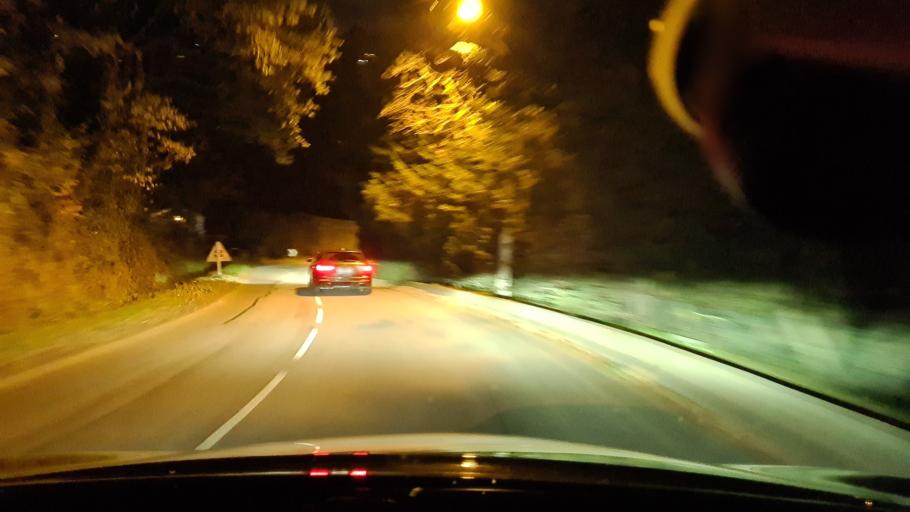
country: FR
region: Rhone-Alpes
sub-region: Departement du Rhone
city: Limonest
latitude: 45.8278
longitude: 4.7853
